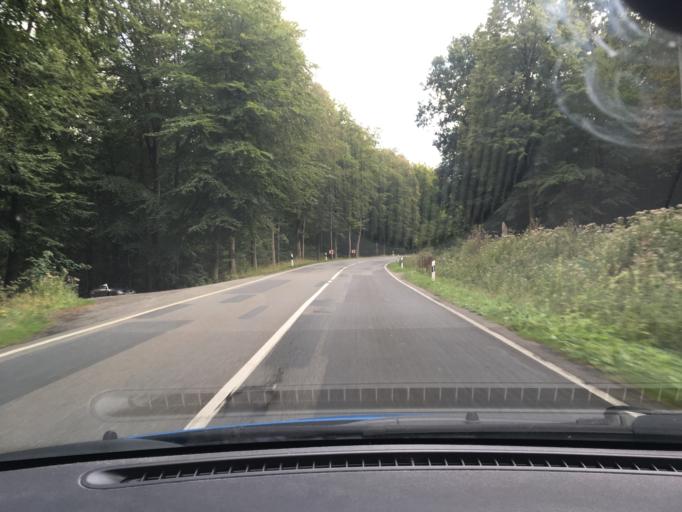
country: DE
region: Lower Saxony
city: Egestorf
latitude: 52.2772
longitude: 9.4949
